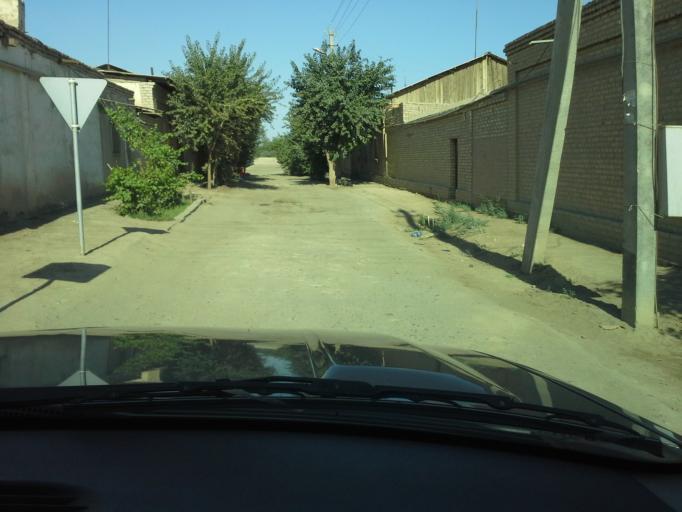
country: TM
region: Dasoguz
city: Dasoguz
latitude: 41.8271
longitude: 59.9793
